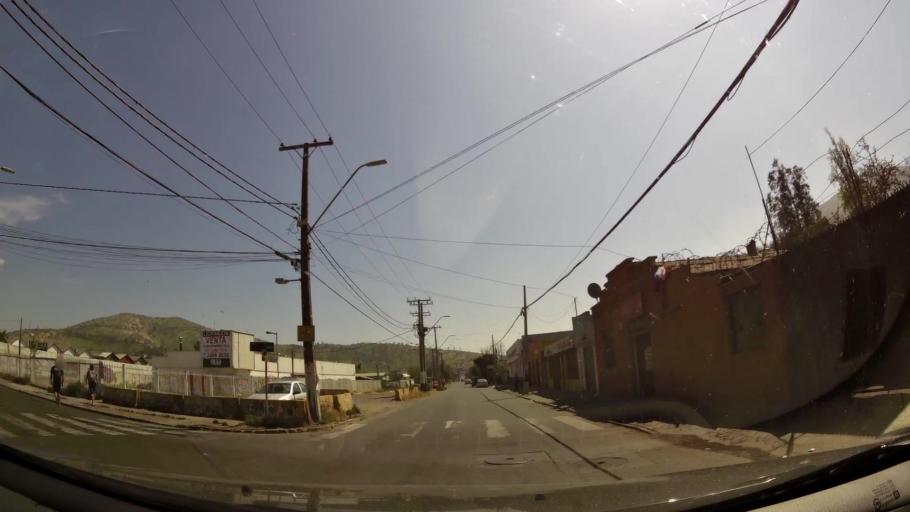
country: CL
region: Santiago Metropolitan
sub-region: Provincia de Santiago
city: Lo Prado
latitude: -33.4007
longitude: -70.7214
